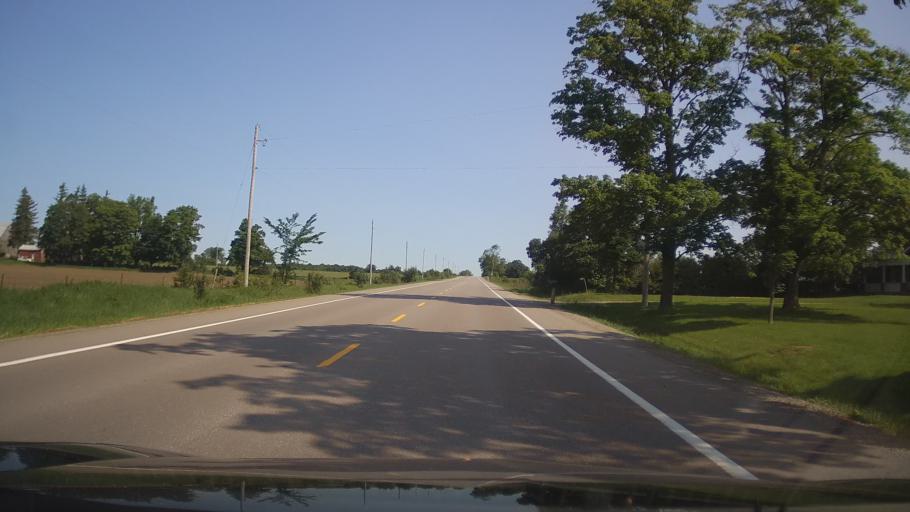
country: CA
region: Ontario
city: Omemee
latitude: 44.3623
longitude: -78.8928
